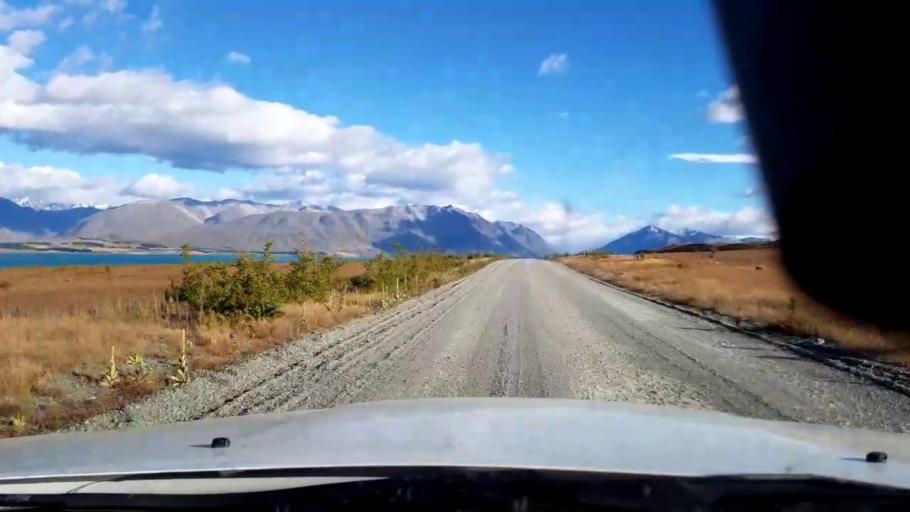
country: NZ
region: Canterbury
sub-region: Timaru District
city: Pleasant Point
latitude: -43.9167
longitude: 170.5582
